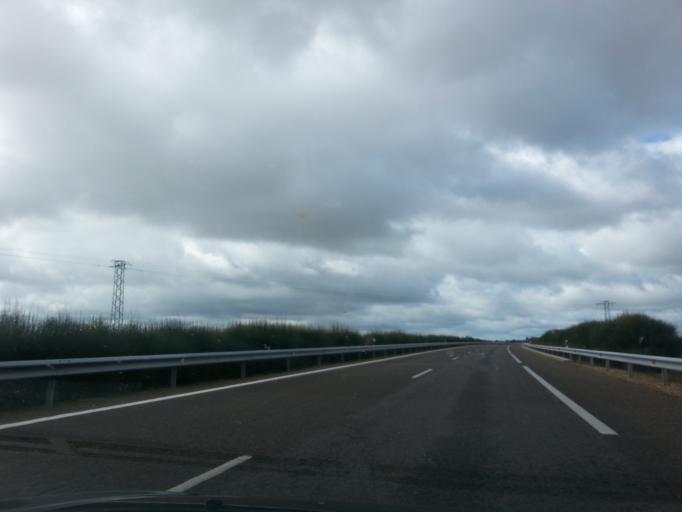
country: ES
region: Castille and Leon
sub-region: Provincia de Salamanca
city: La Fuente de San Esteban
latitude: 40.7954
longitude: -6.2129
